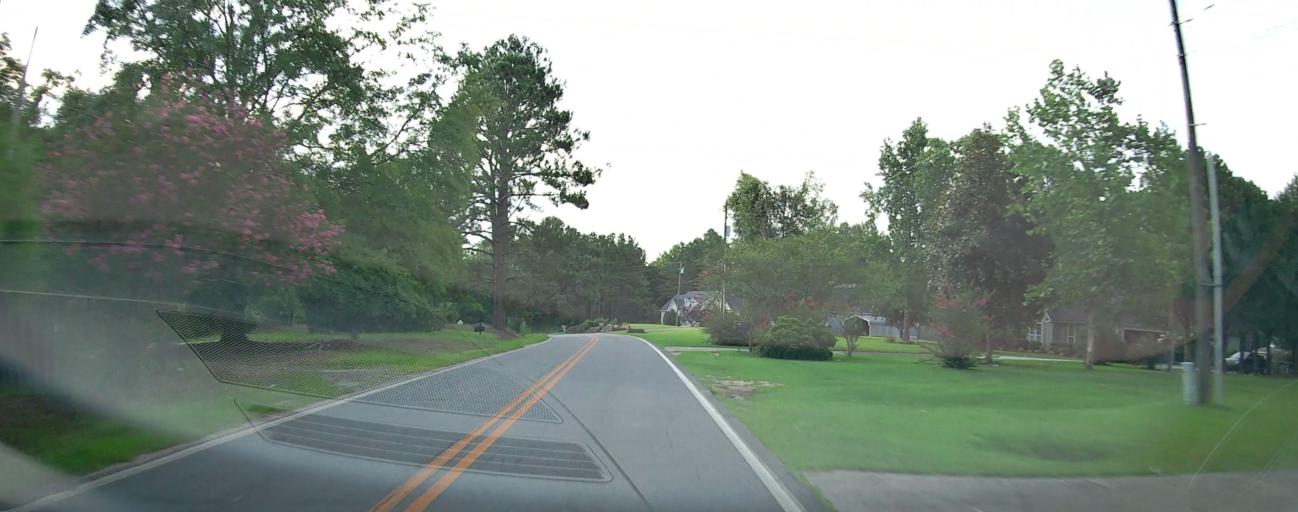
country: US
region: Georgia
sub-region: Peach County
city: Byron
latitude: 32.7220
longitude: -83.7564
